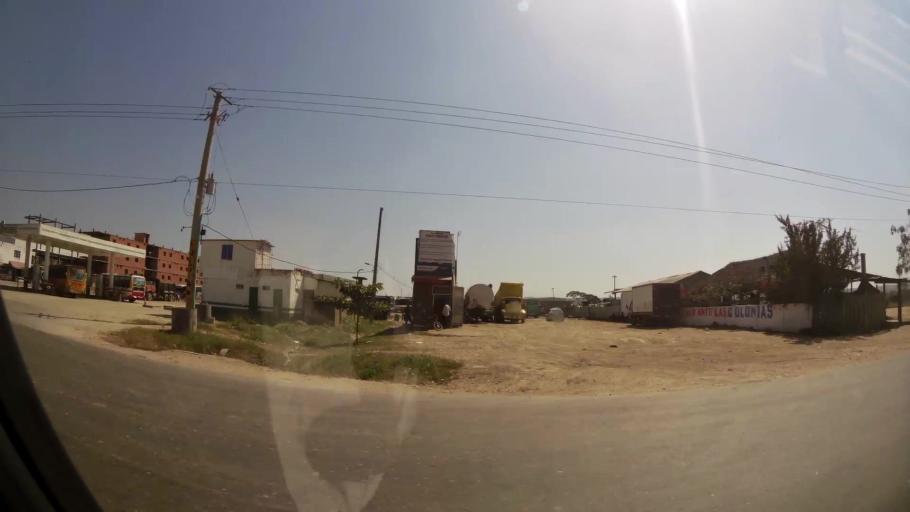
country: CO
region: Bolivar
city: Cartagena
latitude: 10.3880
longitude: -75.4493
